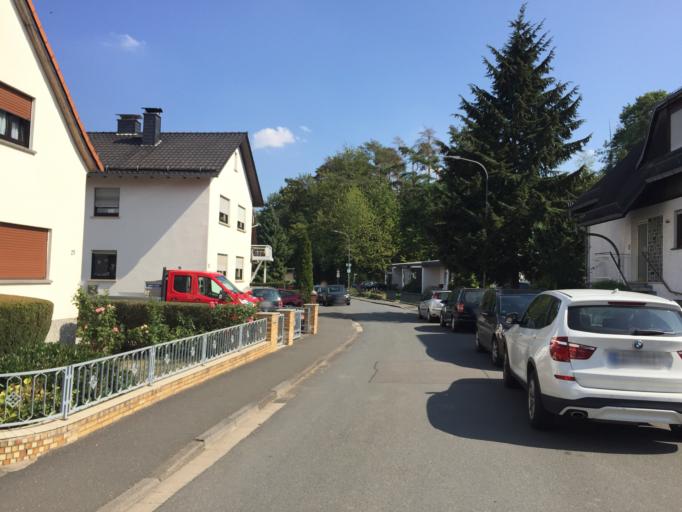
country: DE
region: Hesse
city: Solms
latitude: 50.5396
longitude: 8.4157
